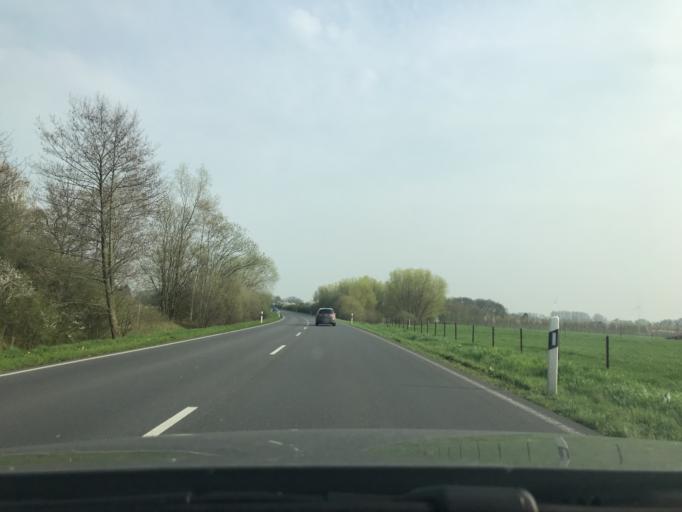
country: DE
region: North Rhine-Westphalia
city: Geldern
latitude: 51.5093
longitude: 6.2978
